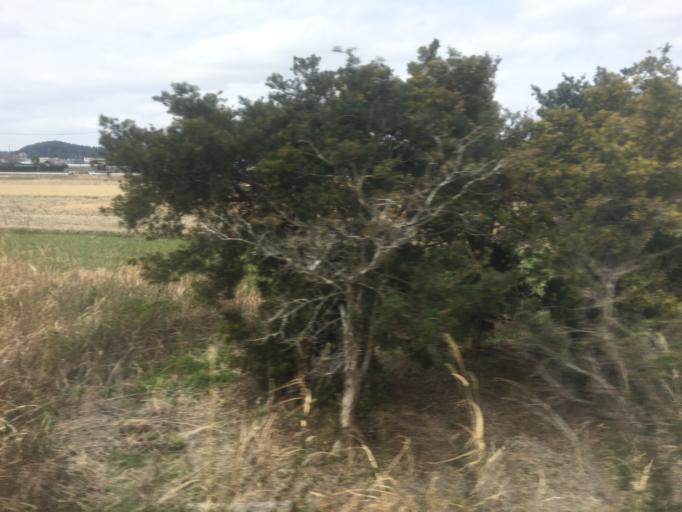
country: JP
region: Chiba
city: Naruto
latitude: 35.5927
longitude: 140.4107
